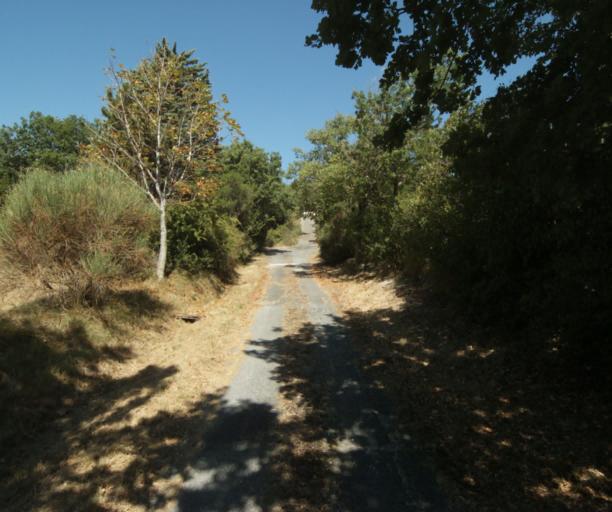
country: FR
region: Midi-Pyrenees
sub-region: Departement de la Haute-Garonne
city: Revel
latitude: 43.5109
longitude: 1.9478
